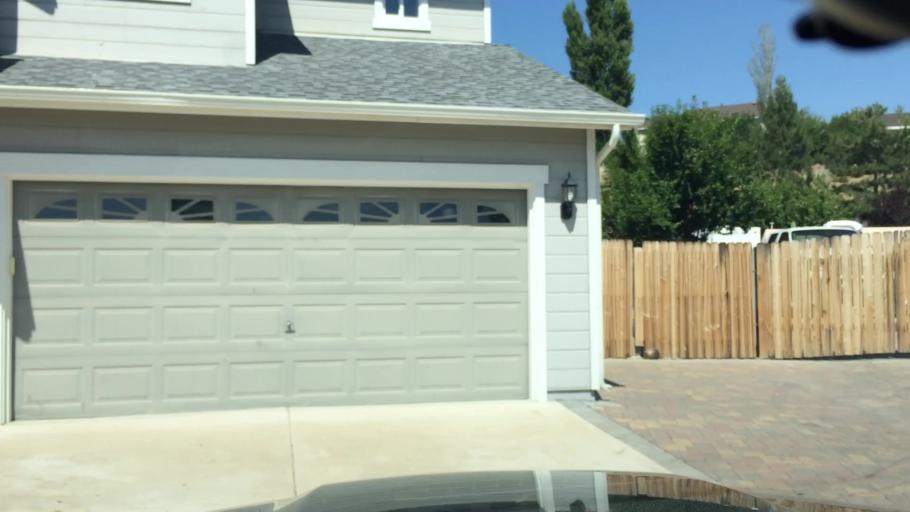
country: US
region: Nevada
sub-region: Washoe County
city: Sparks
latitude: 39.5716
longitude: -119.6925
